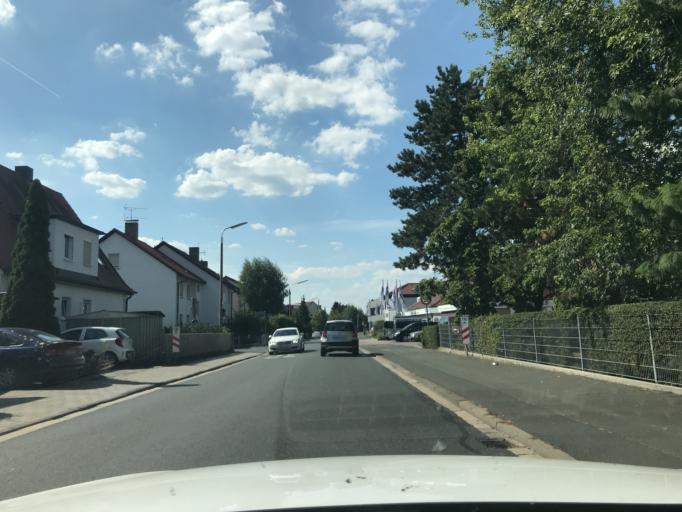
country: DE
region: Bavaria
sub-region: Regierungsbezirk Mittelfranken
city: Erlangen
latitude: 49.5675
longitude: 10.9944
